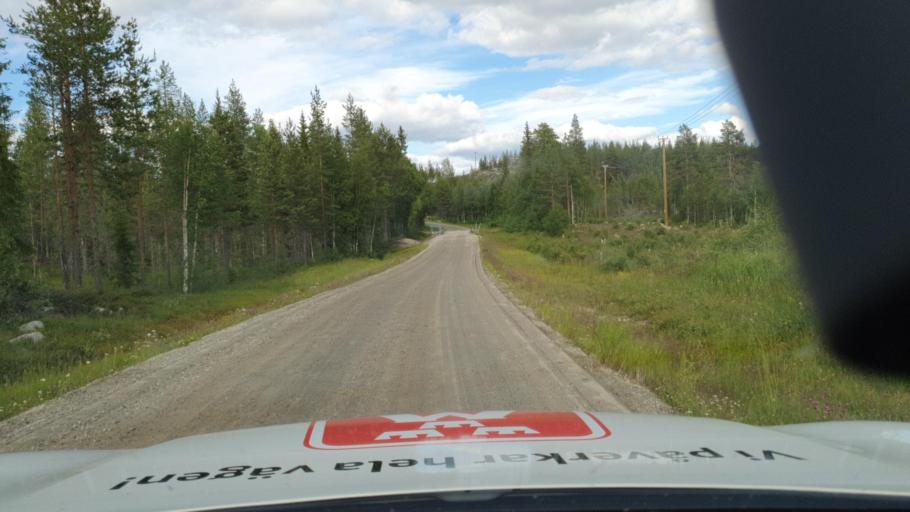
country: SE
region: Vaesterbotten
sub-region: Asele Kommun
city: Insjon
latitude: 64.2471
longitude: 18.0218
